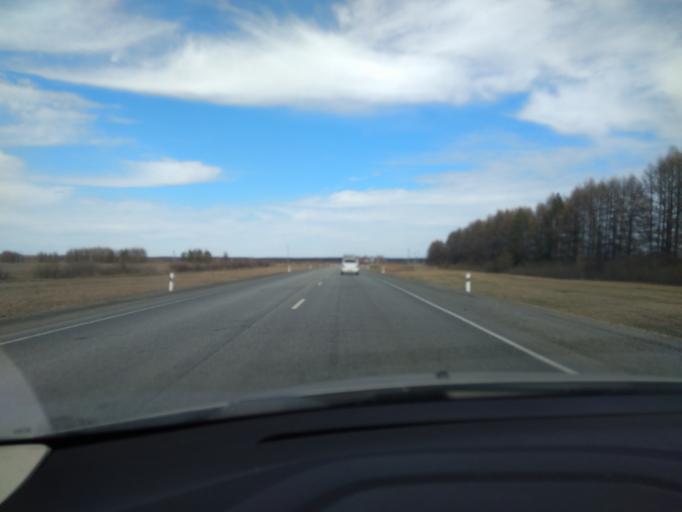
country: RU
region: Sverdlovsk
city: Pyshma
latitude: 57.0403
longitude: 63.4303
